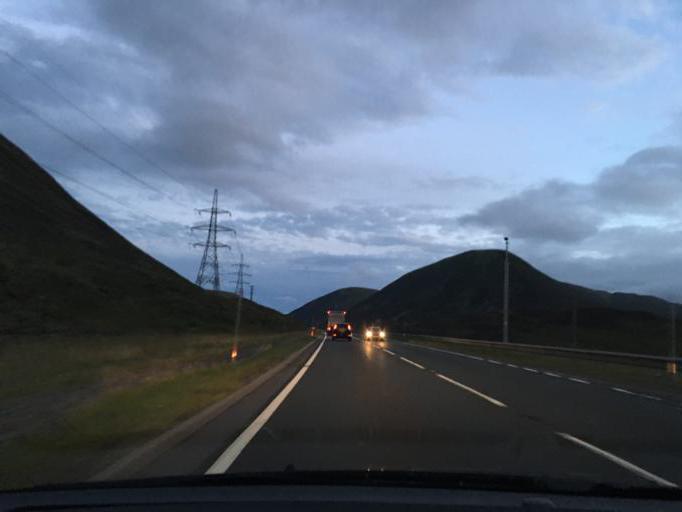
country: GB
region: Scotland
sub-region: Highland
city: Kingussie
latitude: 56.8738
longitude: -4.2571
